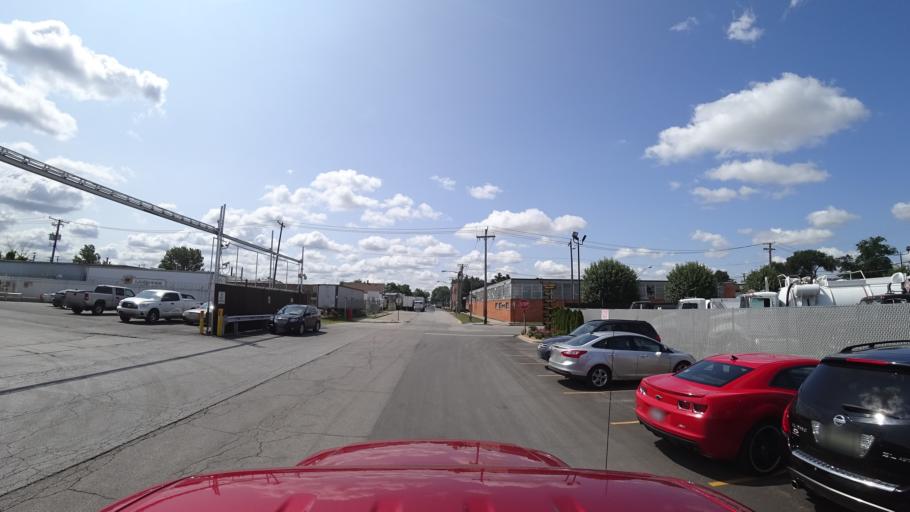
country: US
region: Illinois
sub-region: Cook County
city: Cicero
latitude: 41.8153
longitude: -87.7397
